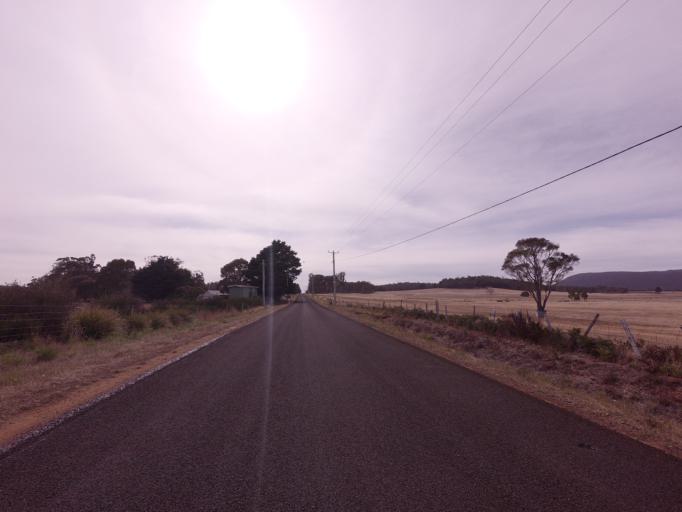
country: AU
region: Tasmania
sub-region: Sorell
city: Sorell
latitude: -42.4294
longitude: 147.4705
